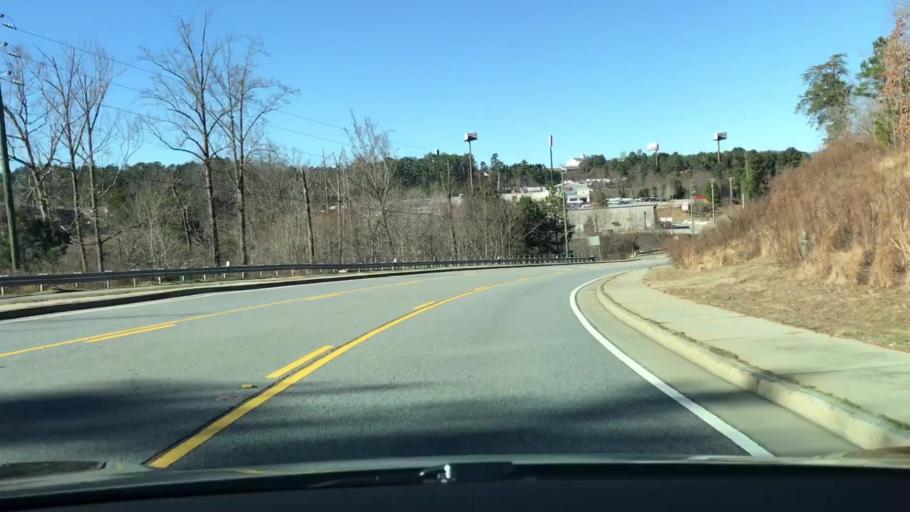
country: US
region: Georgia
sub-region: Forsyth County
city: Cumming
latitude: 34.1877
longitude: -84.1284
